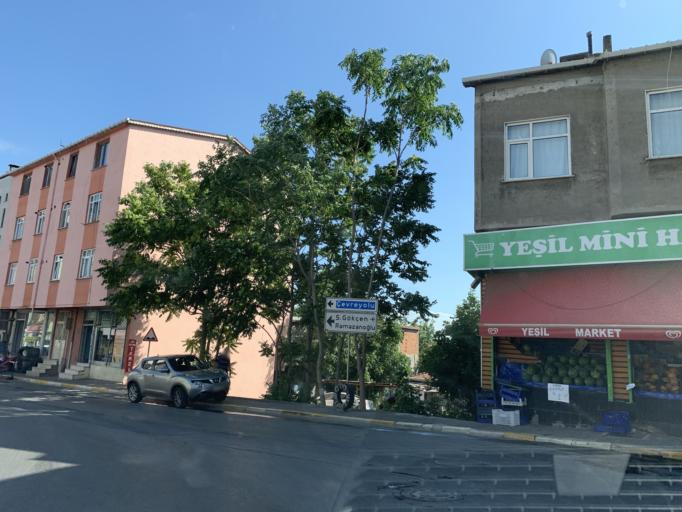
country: TR
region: Istanbul
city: Pendik
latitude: 40.8746
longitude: 29.2799
